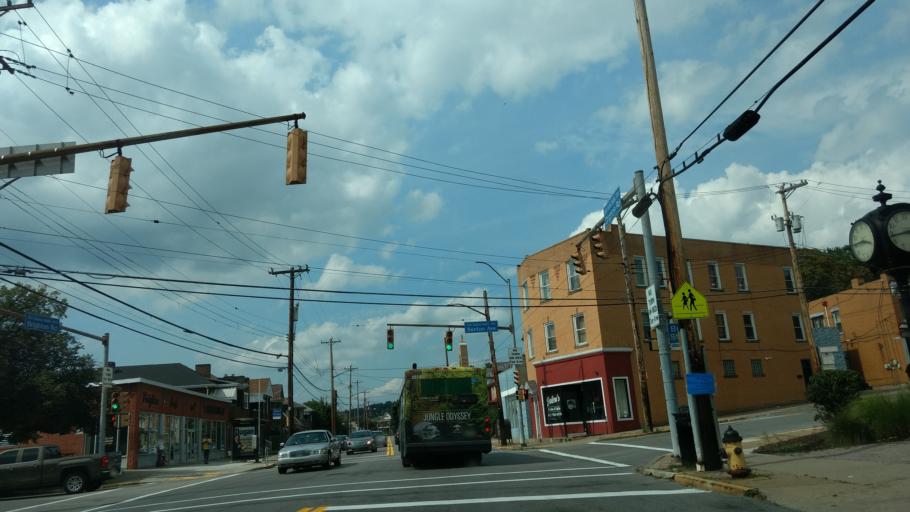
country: US
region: Pennsylvania
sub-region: Allegheny County
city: Bellevue
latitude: 40.4842
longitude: -80.0358
